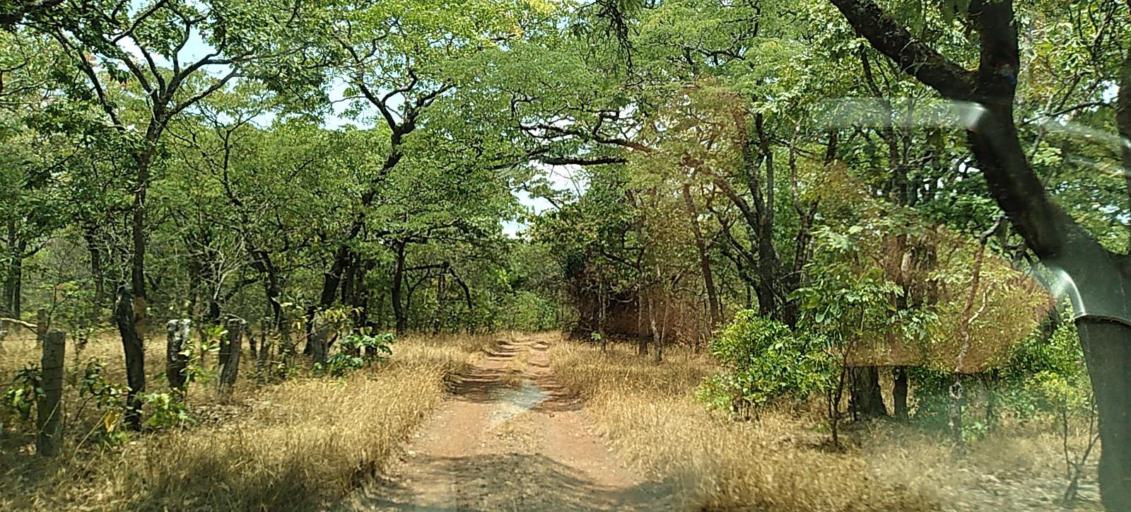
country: ZM
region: Copperbelt
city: Chililabombwe
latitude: -12.4527
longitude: 27.6974
